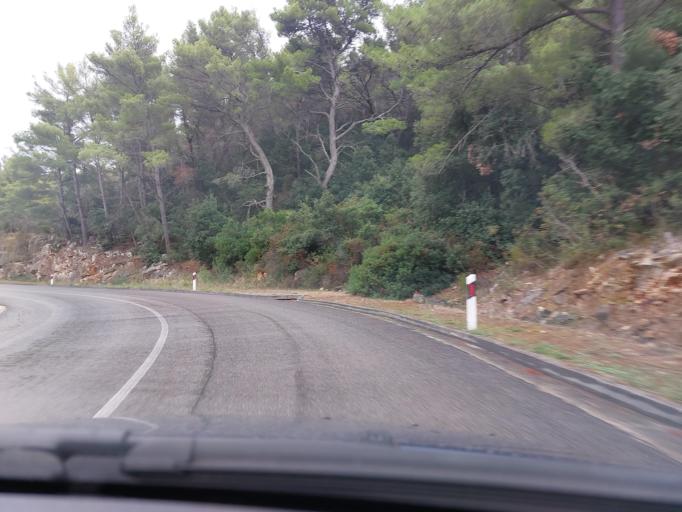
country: HR
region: Dubrovacko-Neretvanska
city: Smokvica
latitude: 42.7667
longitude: 16.8852
